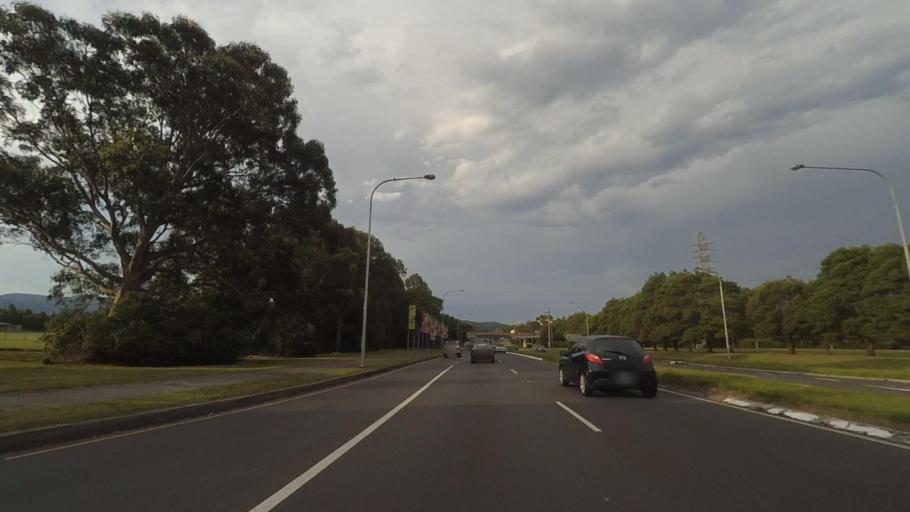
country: AU
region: New South Wales
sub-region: Wollongong
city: Cringila
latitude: -34.4650
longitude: 150.8716
